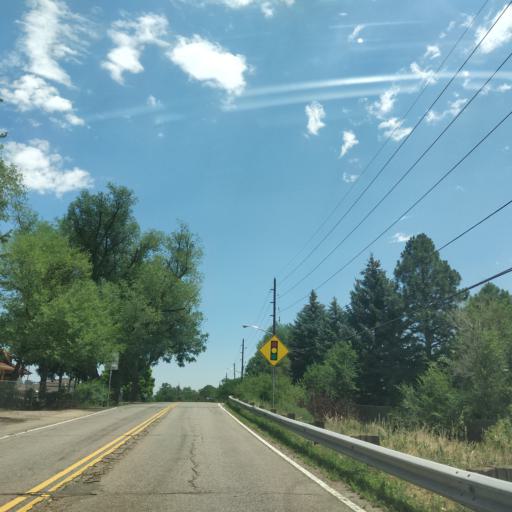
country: US
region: Colorado
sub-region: Jefferson County
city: Lakewood
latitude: 39.6749
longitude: -105.0840
